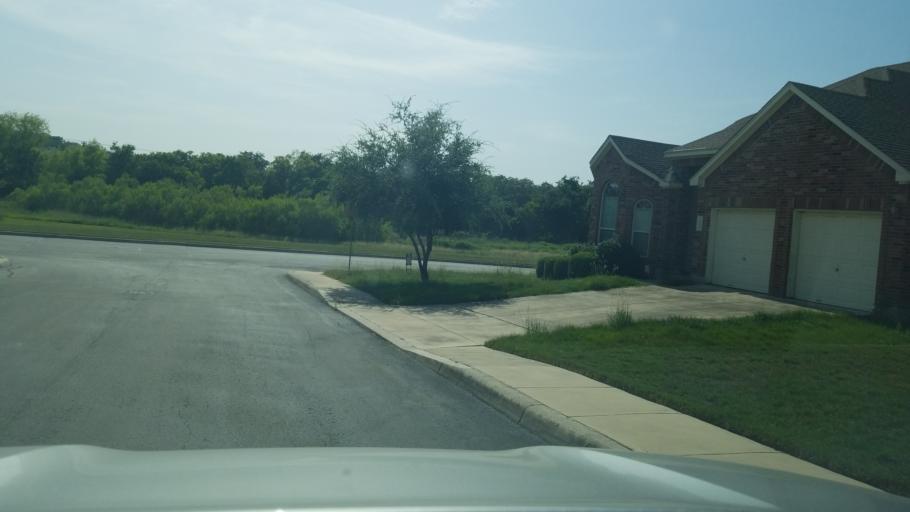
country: US
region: Texas
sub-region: Bexar County
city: Timberwood Park
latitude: 29.6961
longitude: -98.4788
